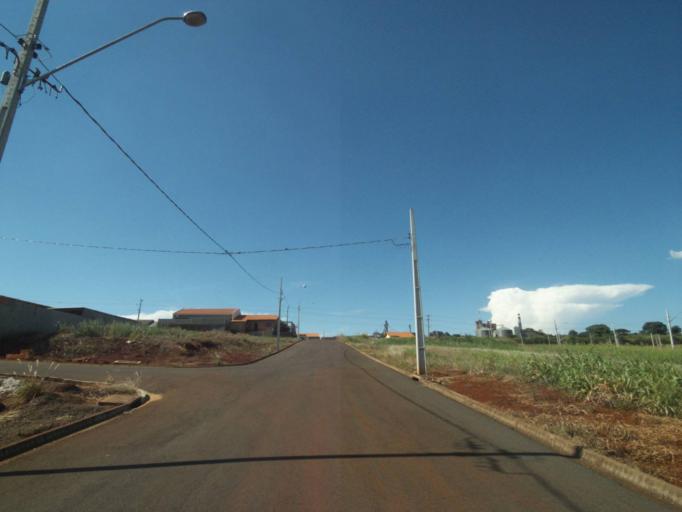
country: BR
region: Parana
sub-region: Sertanopolis
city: Sertanopolis
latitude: -23.0465
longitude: -50.8166
